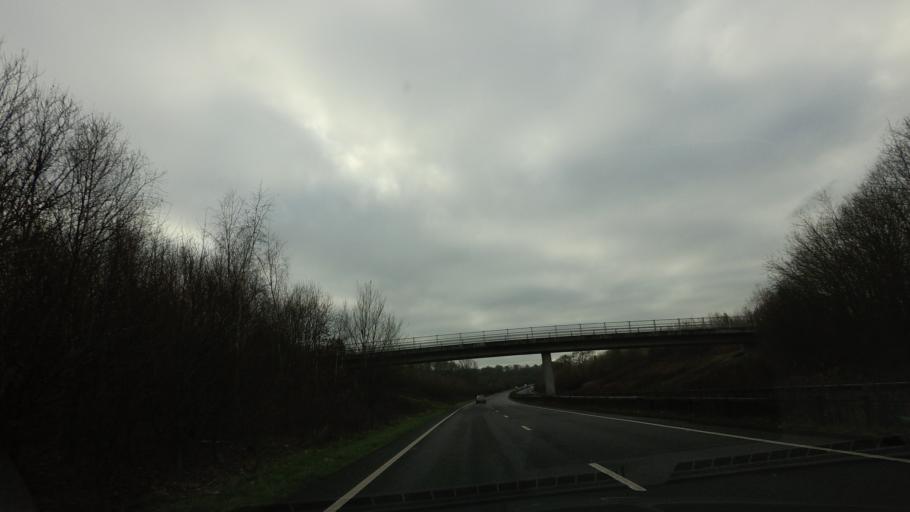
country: GB
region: England
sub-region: East Sussex
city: Wadhurst
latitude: 51.0997
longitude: 0.4036
